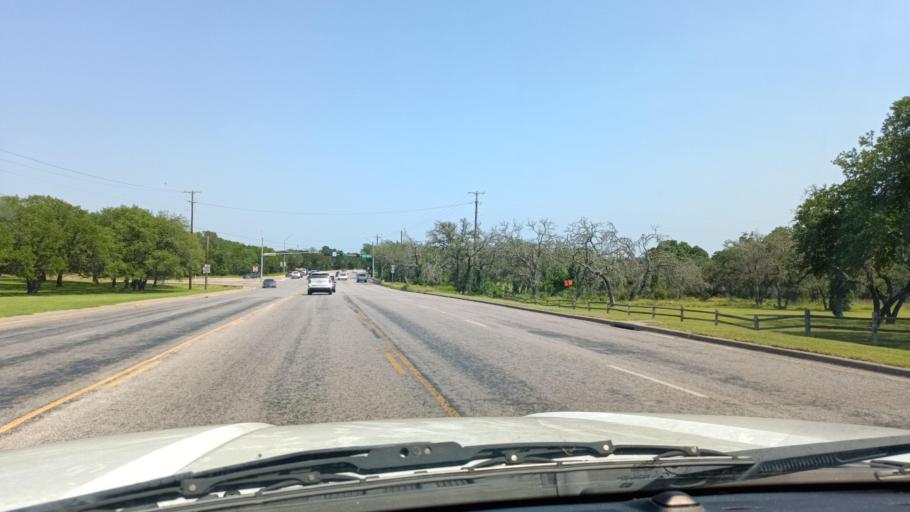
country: US
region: Texas
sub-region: Bell County
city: Morgans Point Resort
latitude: 31.1030
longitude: -97.4784
